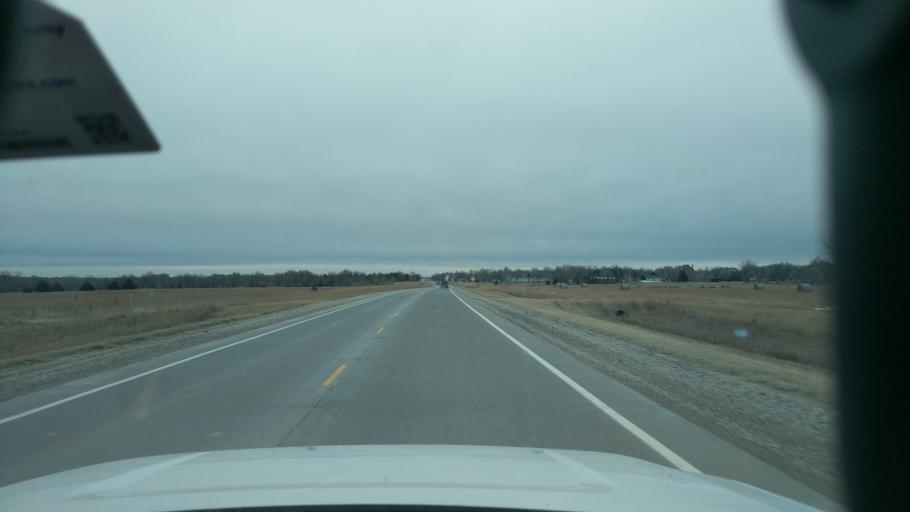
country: US
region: Kansas
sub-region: Marion County
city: Marion
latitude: 38.5013
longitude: -96.9576
